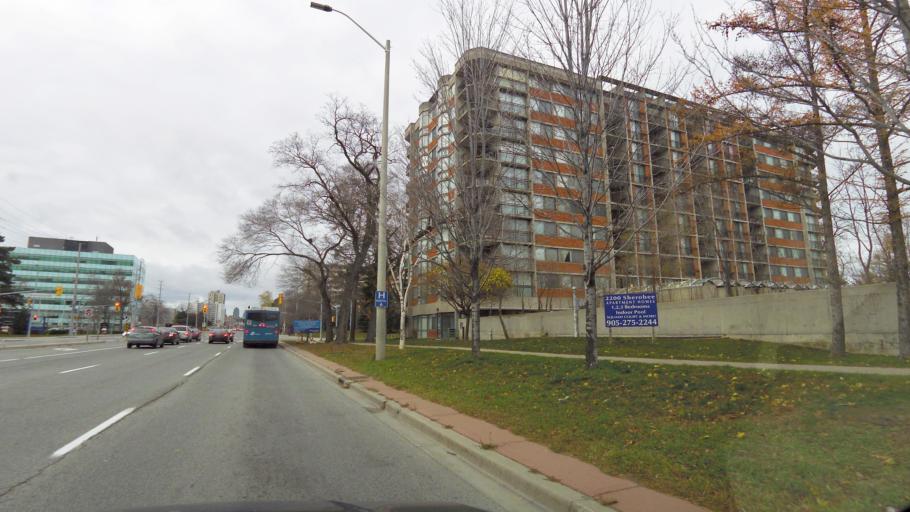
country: CA
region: Ontario
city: Mississauga
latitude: 43.5718
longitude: -79.6040
